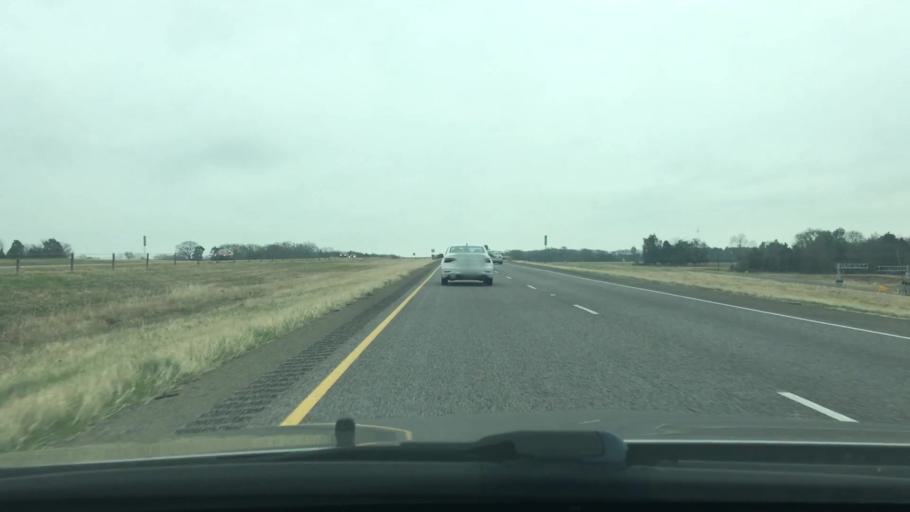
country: US
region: Texas
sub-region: Freestone County
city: Fairfield
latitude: 31.7737
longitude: -96.2243
